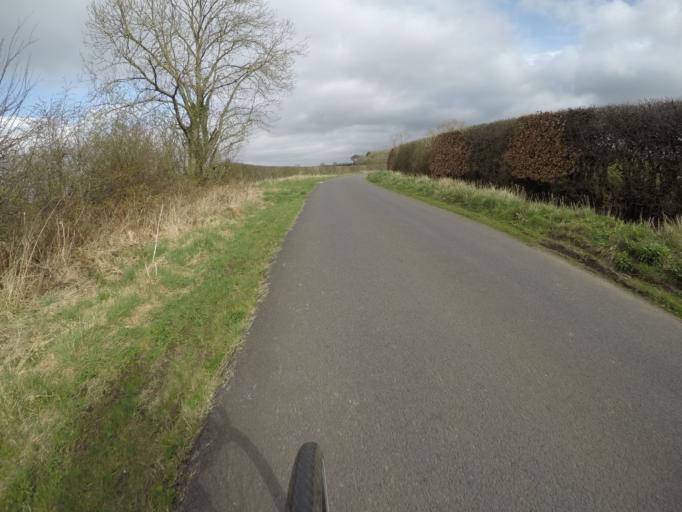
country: GB
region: Scotland
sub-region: North Ayrshire
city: Irvine
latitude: 55.6374
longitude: -4.6312
